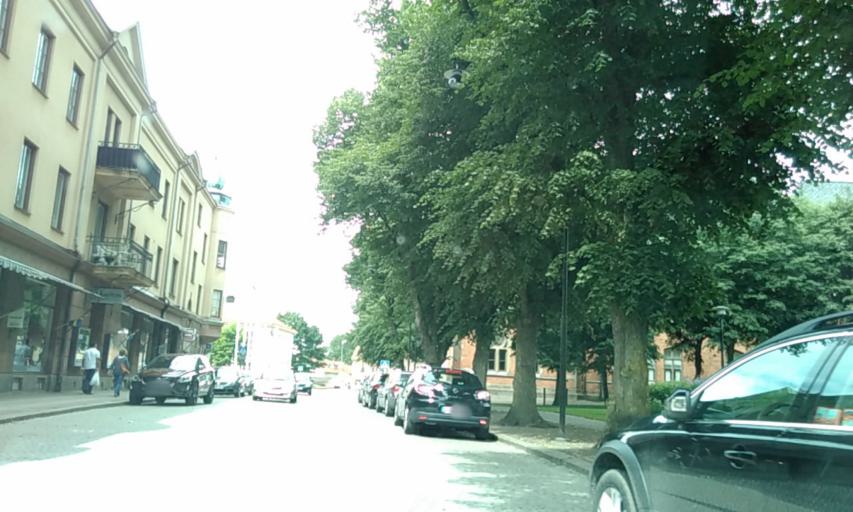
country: SE
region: Vaestra Goetaland
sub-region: Skara Kommun
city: Skara
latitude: 58.3854
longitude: 13.4388
